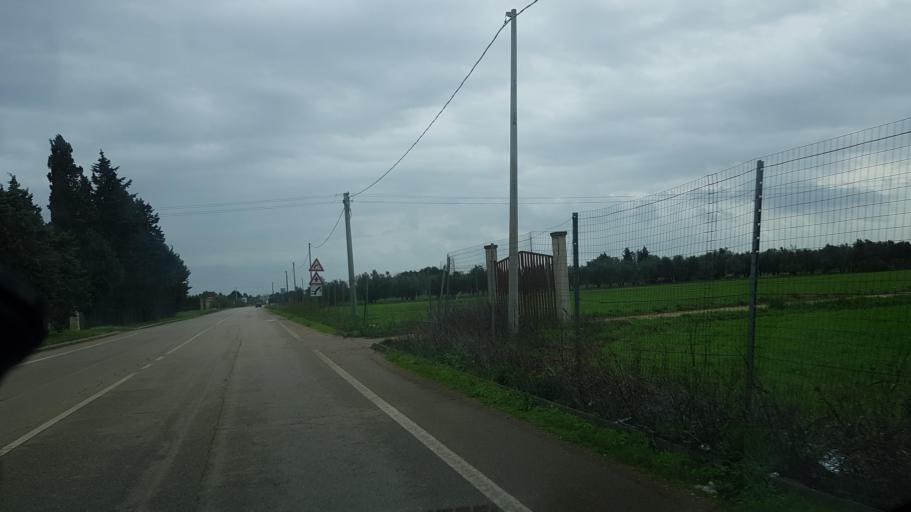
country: IT
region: Apulia
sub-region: Provincia di Lecce
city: Campi Salentina
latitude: 40.3829
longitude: 18.0268
